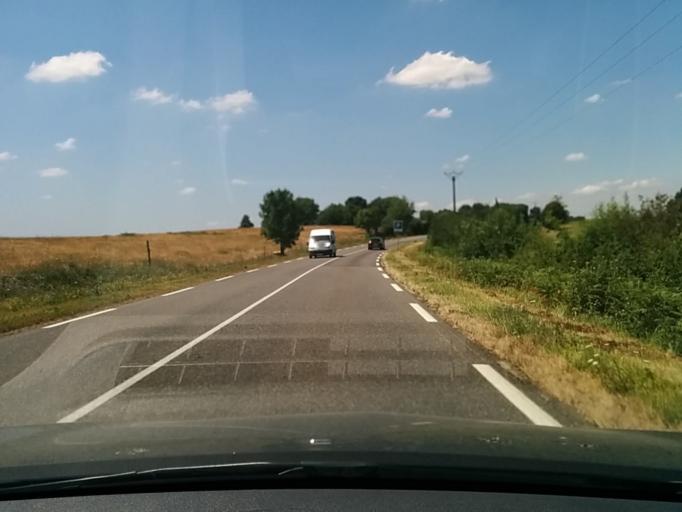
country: FR
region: Midi-Pyrenees
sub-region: Departement du Gers
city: Eauze
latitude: 43.7870
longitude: 0.1079
